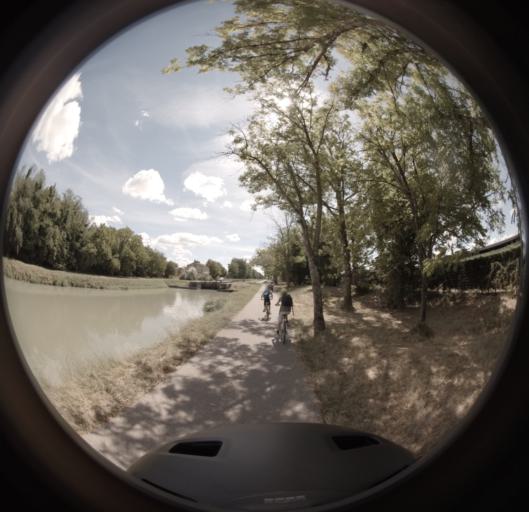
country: FR
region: Midi-Pyrenees
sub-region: Departement du Tarn-et-Garonne
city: Castelsarrasin
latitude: 44.0636
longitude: 1.1022
